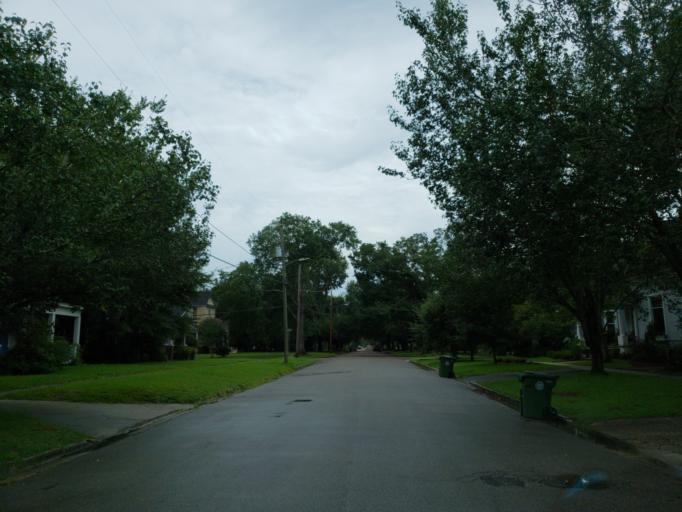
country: US
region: Mississippi
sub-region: Forrest County
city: Hattiesburg
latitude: 31.3210
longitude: -89.2877
